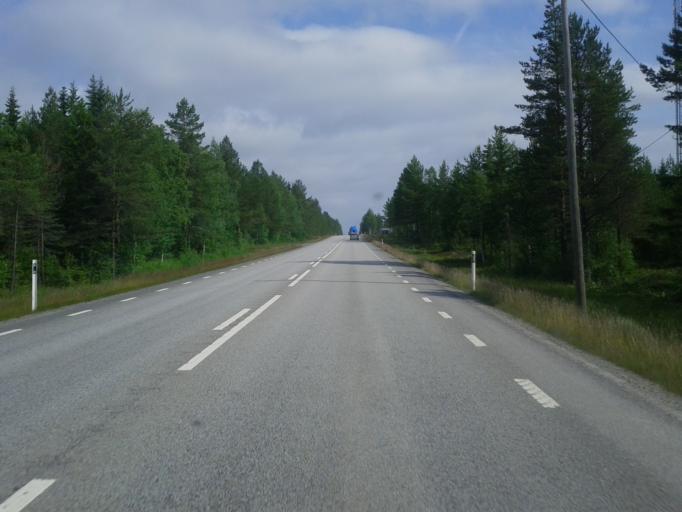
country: SE
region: Vaesterbotten
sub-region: Robertsfors Kommun
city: Robertsfors
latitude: 64.1894
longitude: 20.9982
